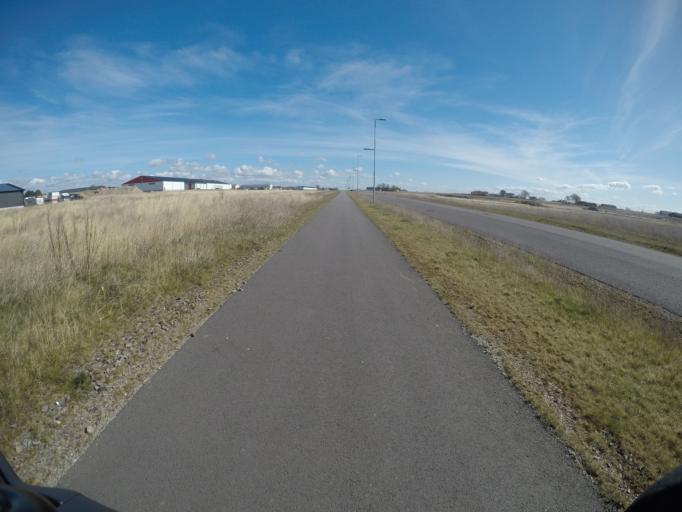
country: SE
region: Halland
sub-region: Laholms Kommun
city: Laholm
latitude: 56.4977
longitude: 13.0084
